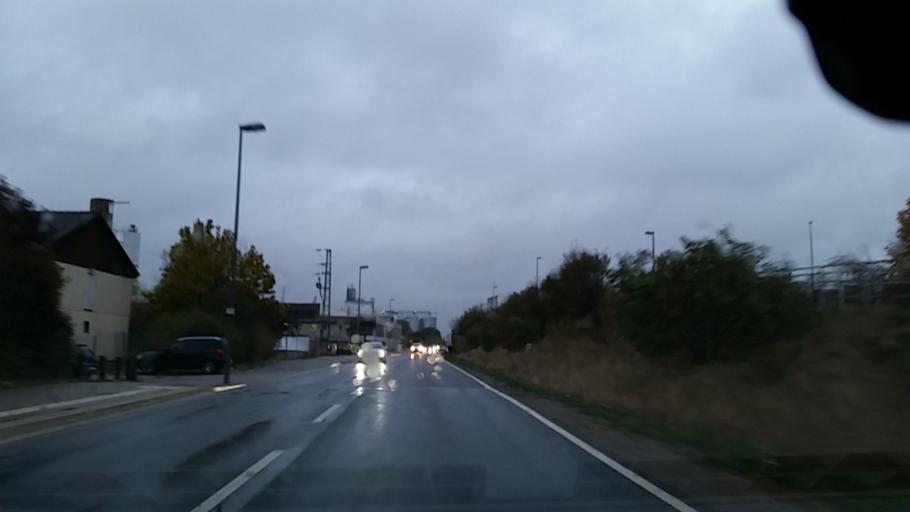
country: DE
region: Lower Saxony
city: Weyhausen
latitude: 52.4240
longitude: 10.7099
